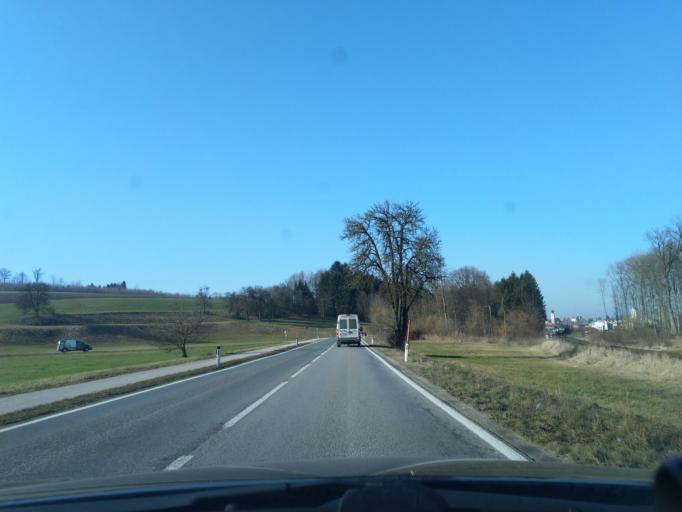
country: AT
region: Upper Austria
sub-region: Politischer Bezirk Ried im Innkreis
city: Ried im Innkreis
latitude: 48.2384
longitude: 13.4620
